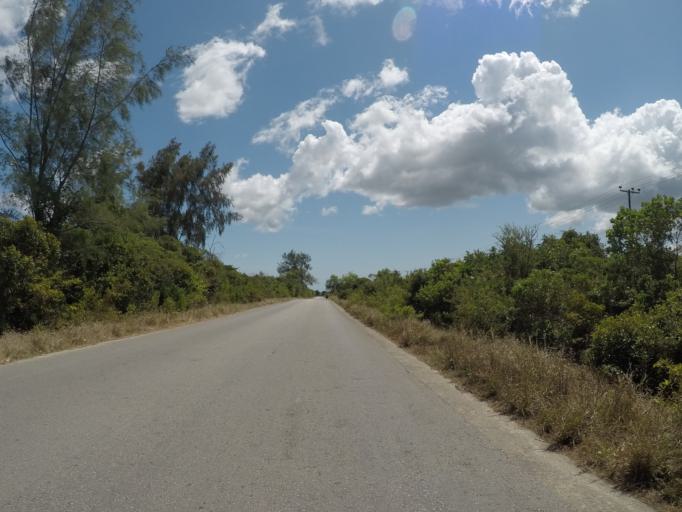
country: TZ
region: Zanzibar Central/South
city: Nganane
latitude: -6.2705
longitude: 39.5068
